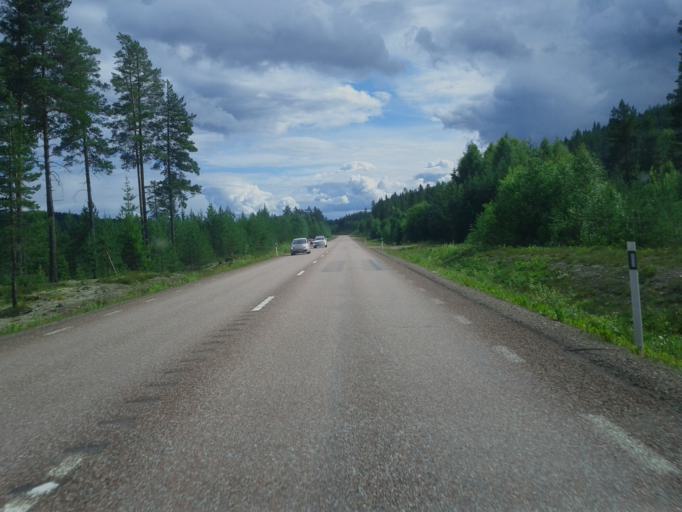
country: SE
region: Dalarna
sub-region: Rattviks Kommun
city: Raettvik
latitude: 60.8093
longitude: 15.2617
